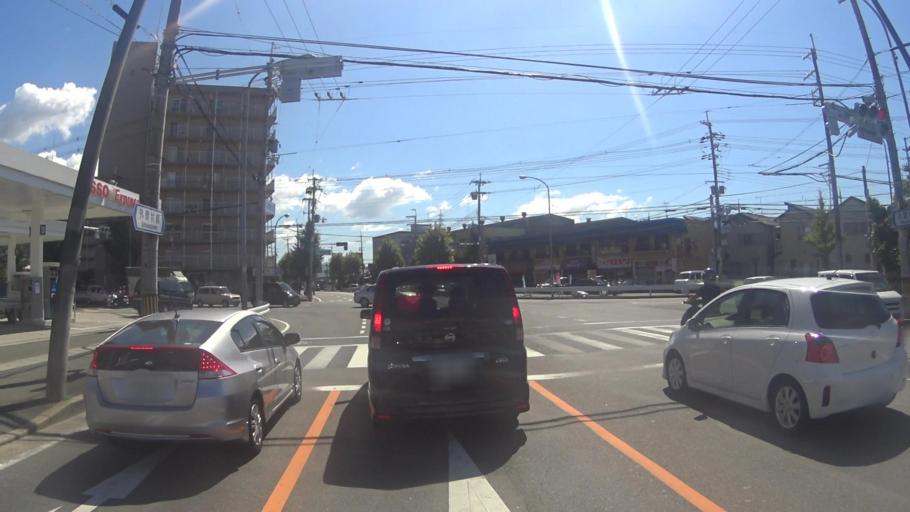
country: JP
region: Kyoto
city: Tanabe
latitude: 34.8368
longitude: 135.7974
